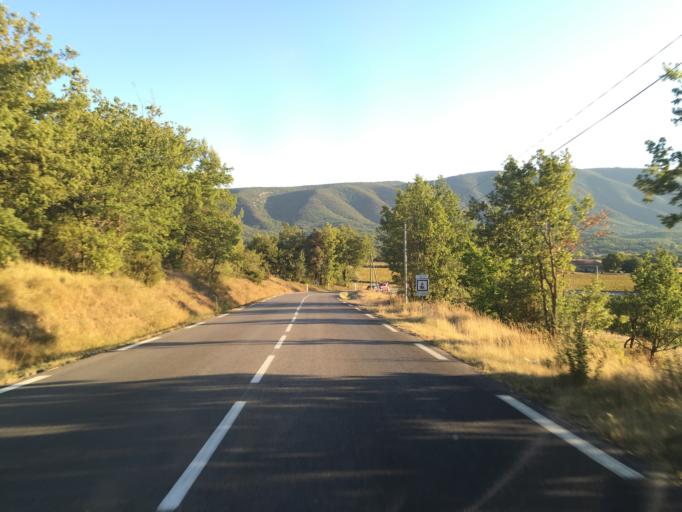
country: FR
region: Provence-Alpes-Cote d'Azur
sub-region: Departement des Alpes-de-Haute-Provence
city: Cereste
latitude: 43.8569
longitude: 5.5648
